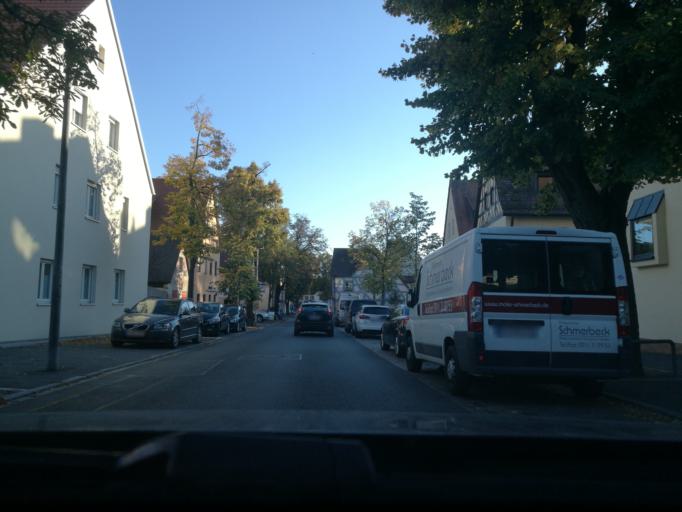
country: DE
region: Bavaria
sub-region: Regierungsbezirk Mittelfranken
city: Furth
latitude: 49.5289
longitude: 11.0110
